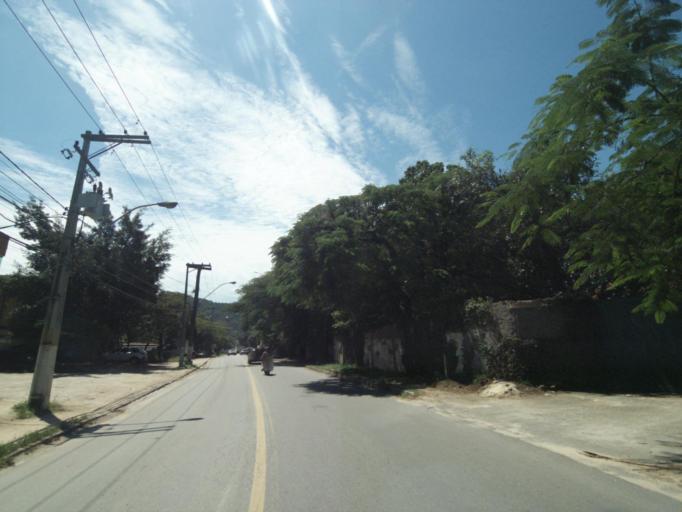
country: BR
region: Rio de Janeiro
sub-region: Niteroi
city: Niteroi
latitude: -22.9303
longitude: -43.0082
